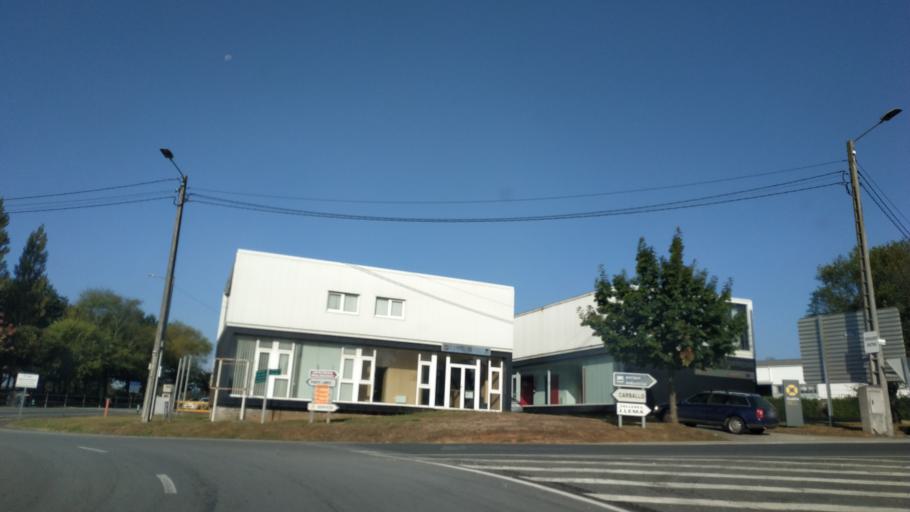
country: ES
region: Galicia
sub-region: Provincia da Coruna
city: Carballo
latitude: 43.2326
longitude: -8.6791
